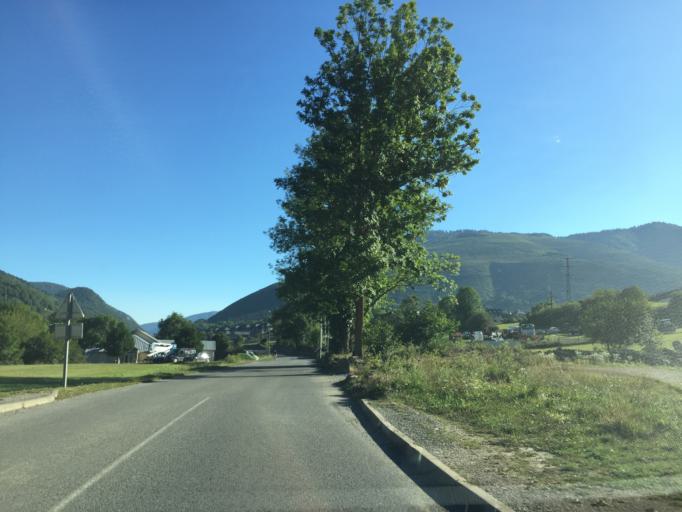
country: FR
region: Midi-Pyrenees
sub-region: Departement des Hautes-Pyrenees
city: Saint-Lary-Soulan
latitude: 42.8960
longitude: 0.3554
